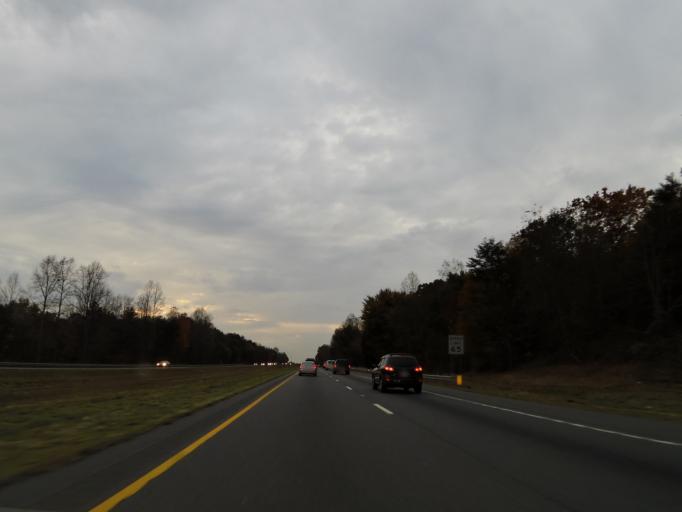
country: US
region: North Carolina
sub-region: Burke County
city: Hildebran
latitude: 35.7059
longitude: -81.4068
